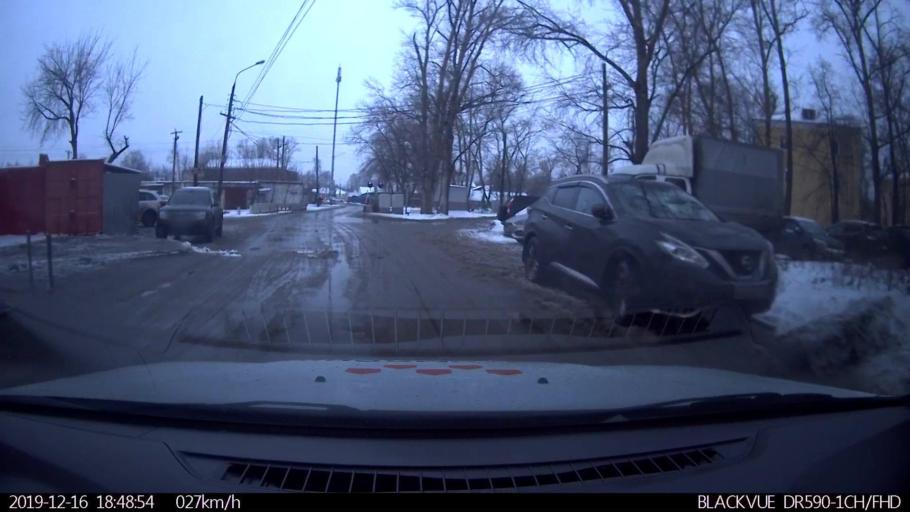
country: RU
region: Nizjnij Novgorod
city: Nizhniy Novgorod
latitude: 56.3048
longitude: 43.9313
